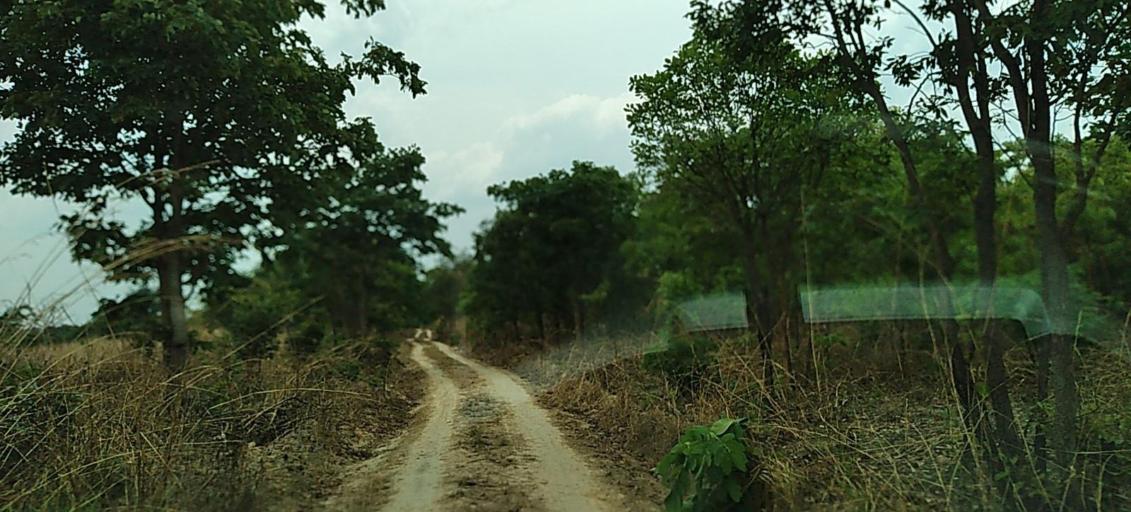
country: ZM
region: Copperbelt
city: Chililabombwe
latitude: -12.3234
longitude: 27.7829
